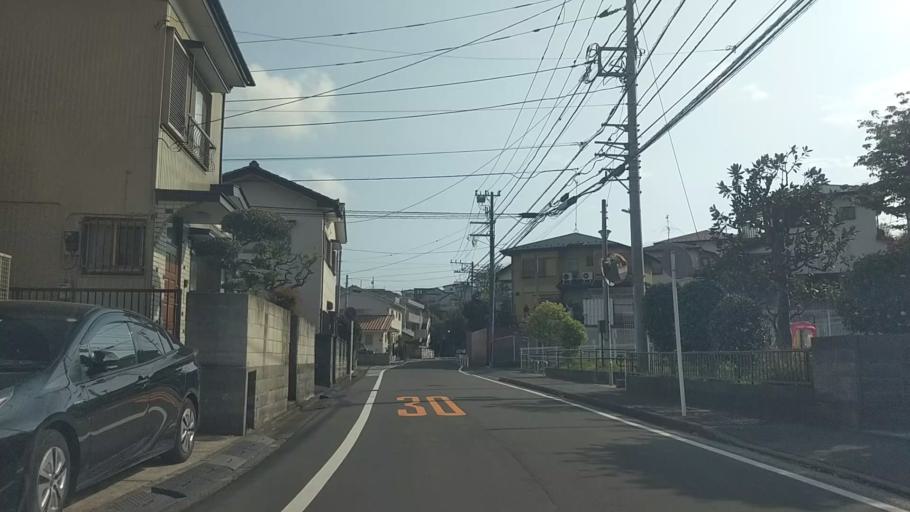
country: JP
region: Kanagawa
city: Kamakura
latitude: 35.3737
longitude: 139.5540
